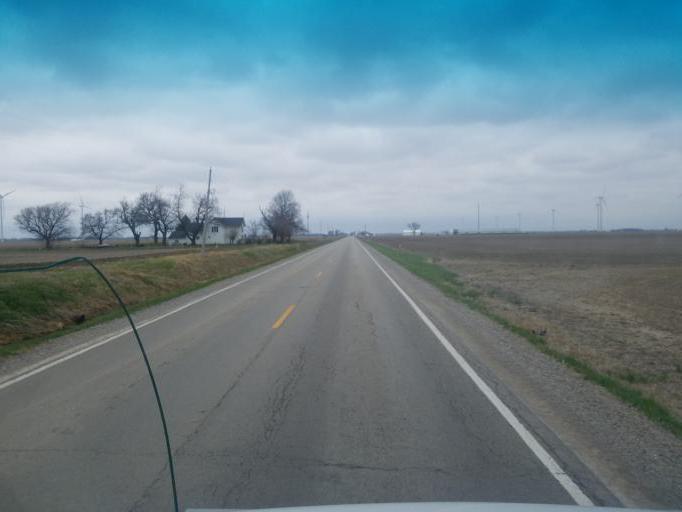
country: US
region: Ohio
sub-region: Paulding County
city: Payne
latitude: 41.0111
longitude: -84.7265
